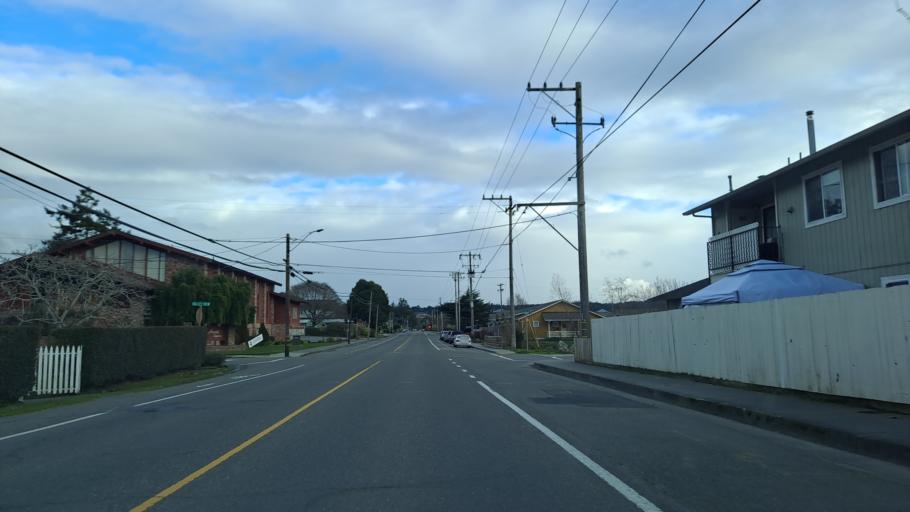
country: US
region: California
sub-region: Humboldt County
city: Fortuna
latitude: 40.5952
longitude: -124.1437
